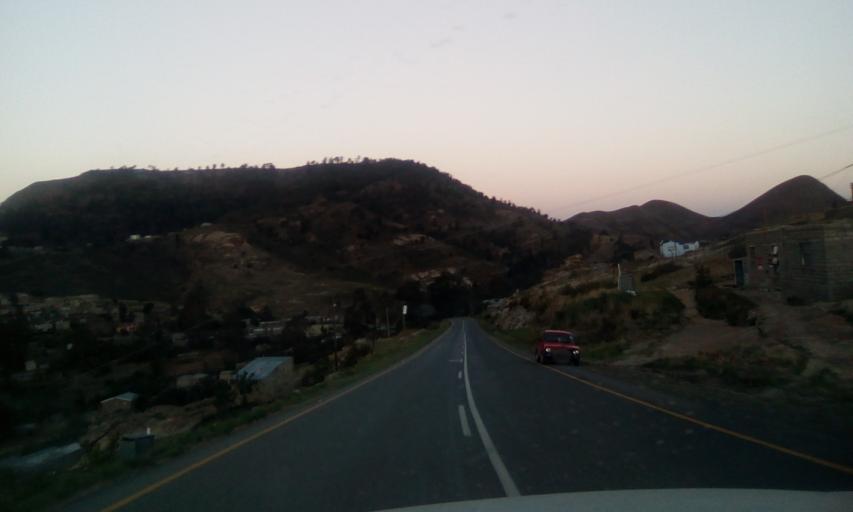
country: LS
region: Qacha's Nek
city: Qacha's Nek
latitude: -30.1284
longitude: 28.6847
